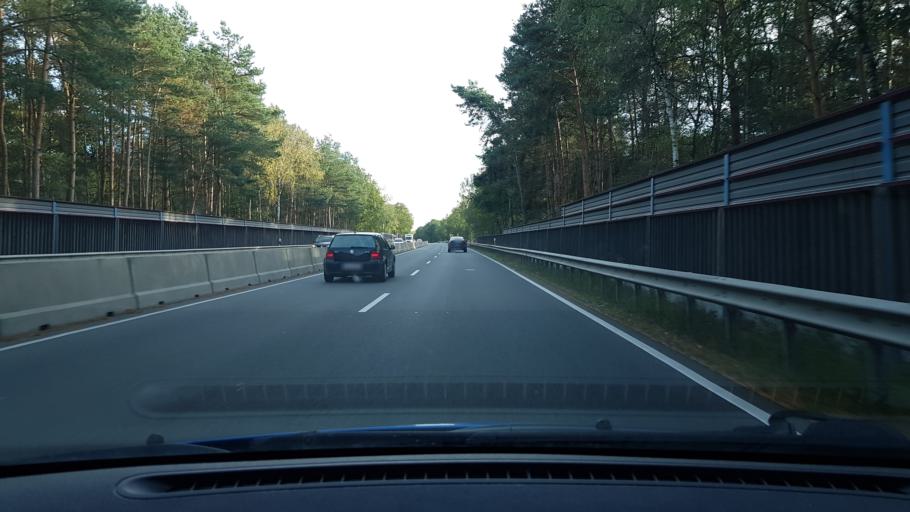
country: DE
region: Lower Saxony
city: Gifhorn
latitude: 52.4594
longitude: 10.5274
